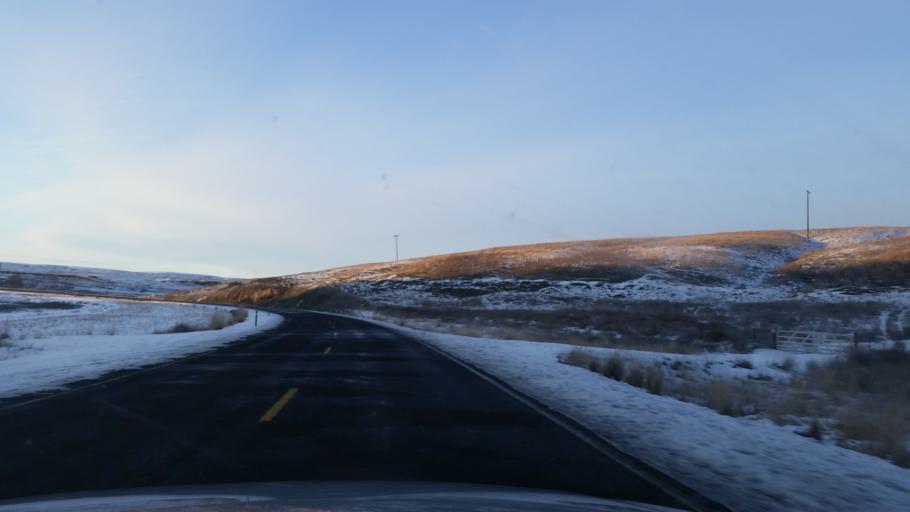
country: US
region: Washington
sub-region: Spokane County
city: Cheney
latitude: 47.1150
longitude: -117.7154
